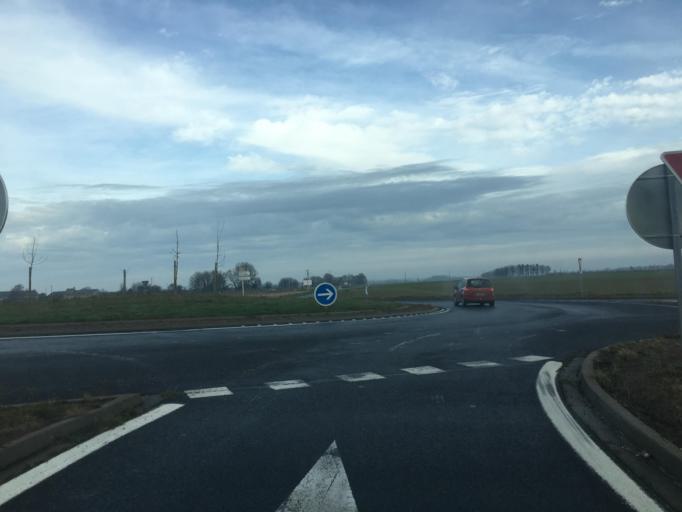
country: FR
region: Lower Normandy
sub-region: Departement du Calvados
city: Creully
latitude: 49.2346
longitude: -0.5779
